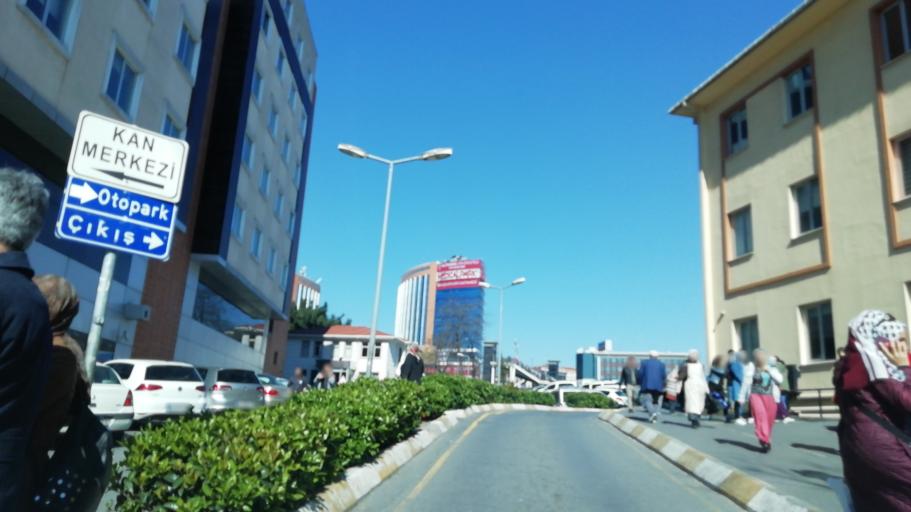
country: TR
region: Istanbul
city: Bahcelievler
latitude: 40.9940
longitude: 28.8654
